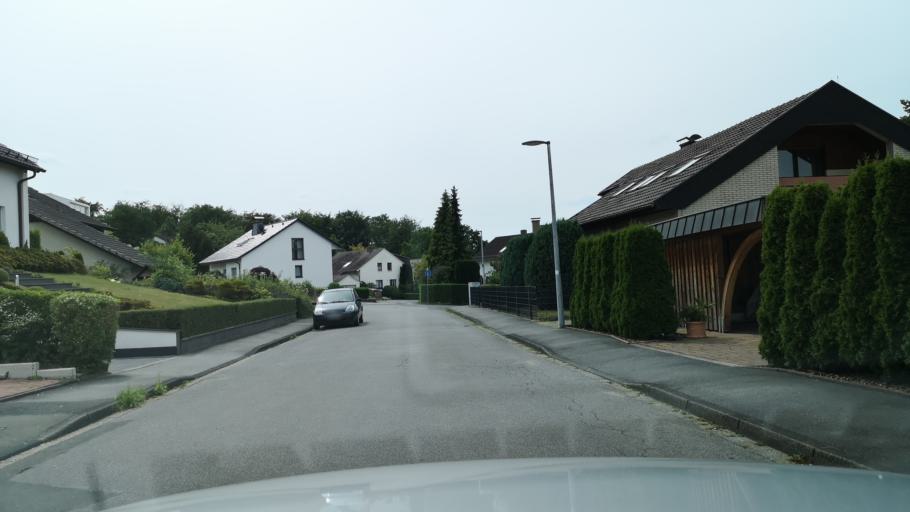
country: DE
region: North Rhine-Westphalia
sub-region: Regierungsbezirk Arnsberg
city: Menden
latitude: 51.4354
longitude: 7.7738
